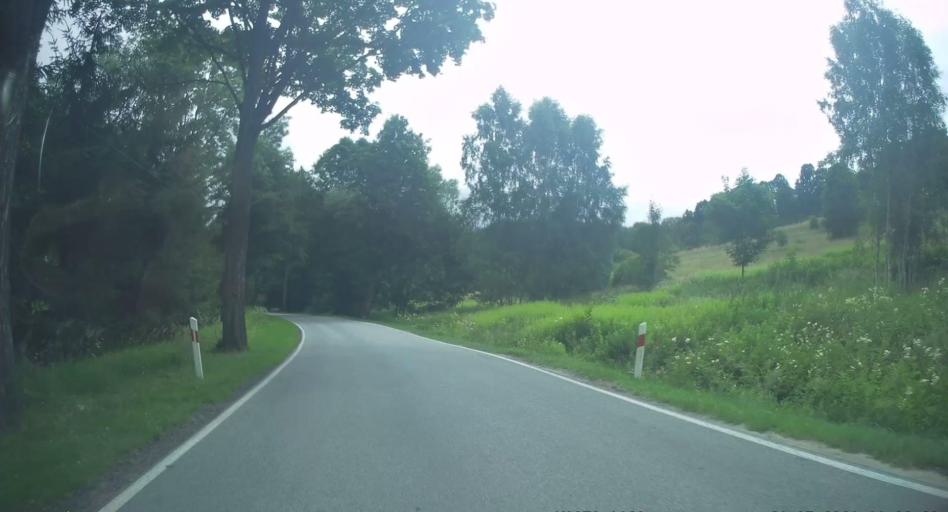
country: PL
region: Lower Silesian Voivodeship
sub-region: Powiat walbrzyski
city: Jedlina-Zdroj
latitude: 50.7290
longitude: 16.3711
